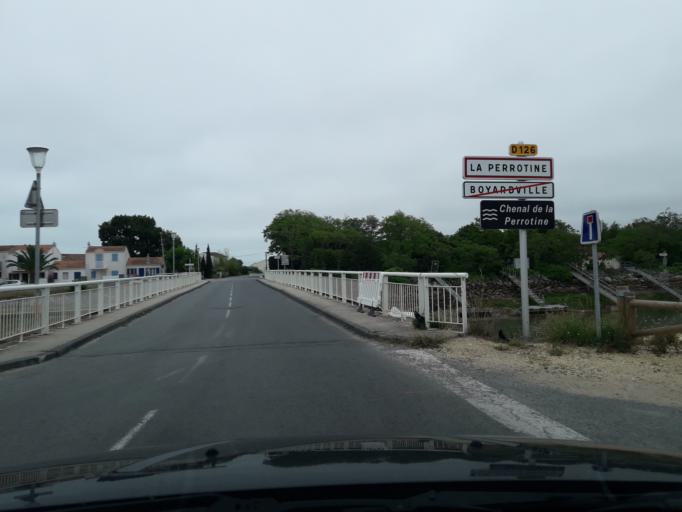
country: FR
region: Poitou-Charentes
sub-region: Departement de la Charente-Maritime
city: Boyard-Ville
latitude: 45.9646
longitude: -1.2447
